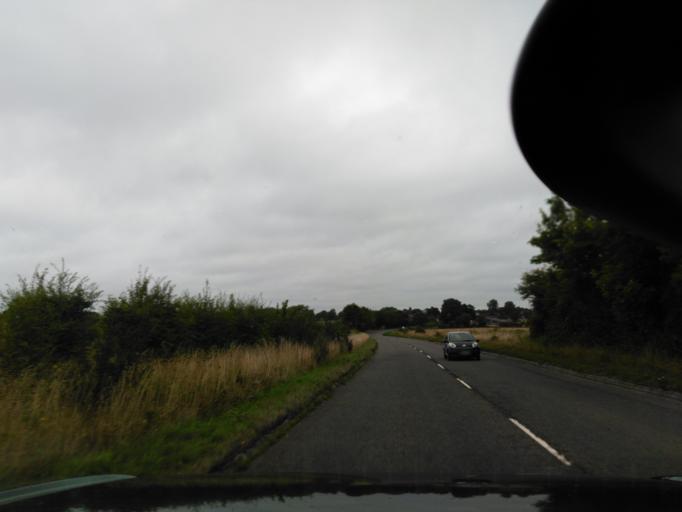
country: GB
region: England
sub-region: Wiltshire
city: Upton Scudamore
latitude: 51.2405
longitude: -2.1882
